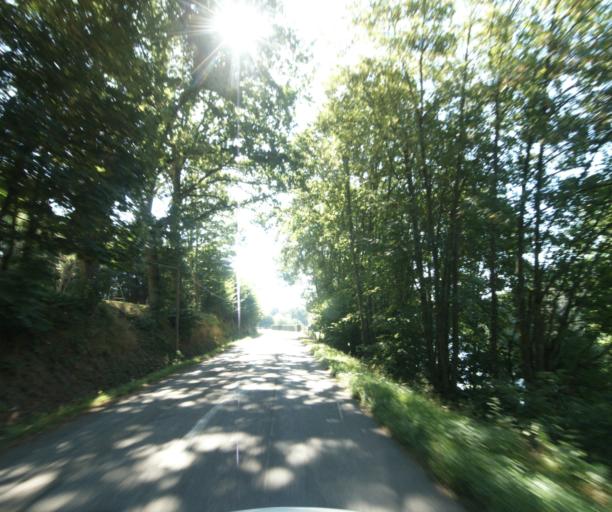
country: FR
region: Lorraine
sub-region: Departement des Vosges
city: Chantraine
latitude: 48.1520
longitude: 6.4600
